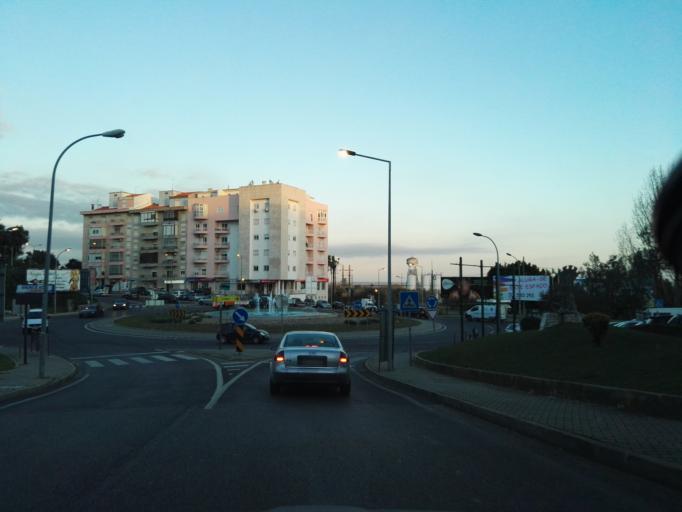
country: PT
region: Lisbon
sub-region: Vila Franca de Xira
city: Povoa de Santa Iria
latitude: 38.8665
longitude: -9.0605
